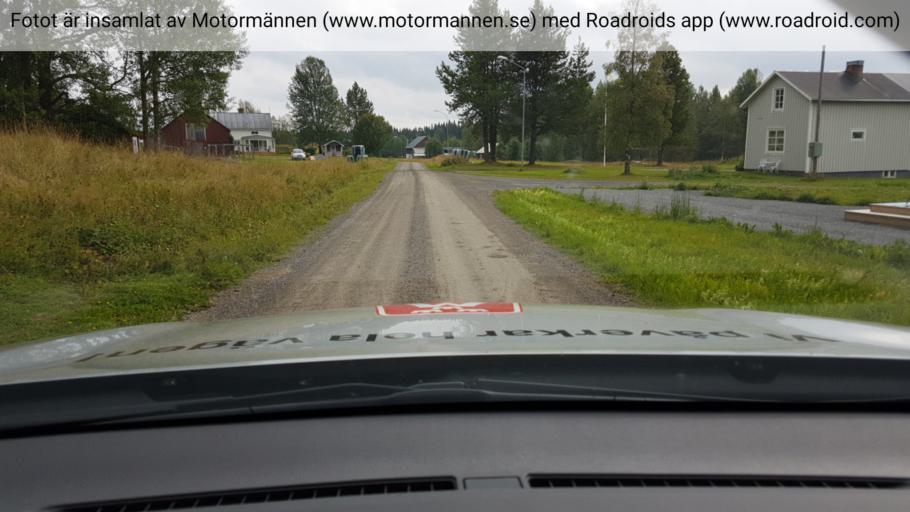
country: SE
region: Jaemtland
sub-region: Stroemsunds Kommun
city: Stroemsund
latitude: 63.7692
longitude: 15.3285
